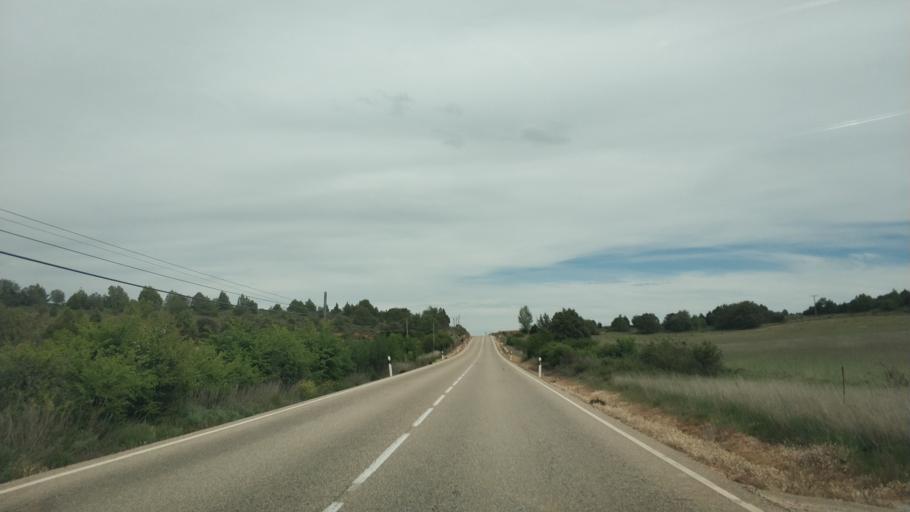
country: ES
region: Castille and Leon
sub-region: Provincia de Soria
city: El Burgo de Osma
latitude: 41.5772
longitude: -3.0299
